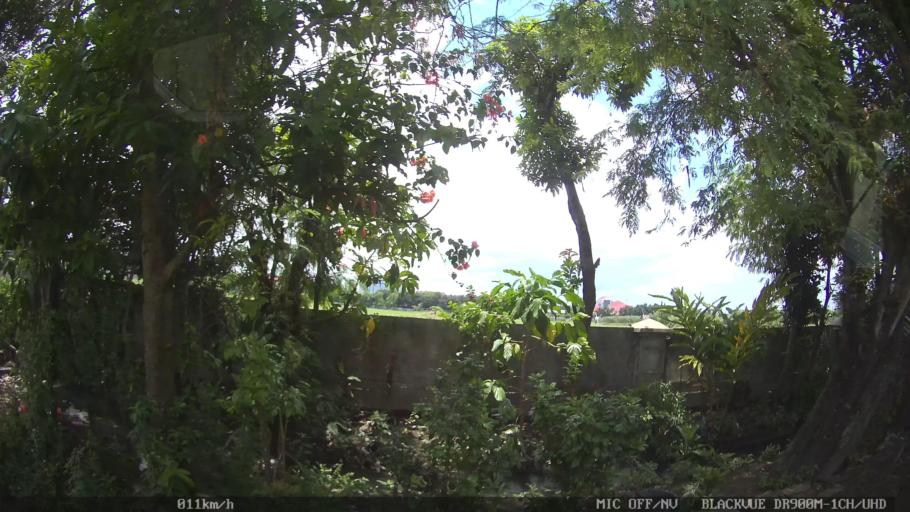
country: ID
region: North Sumatra
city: Medan
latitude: 3.6125
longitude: 98.7213
